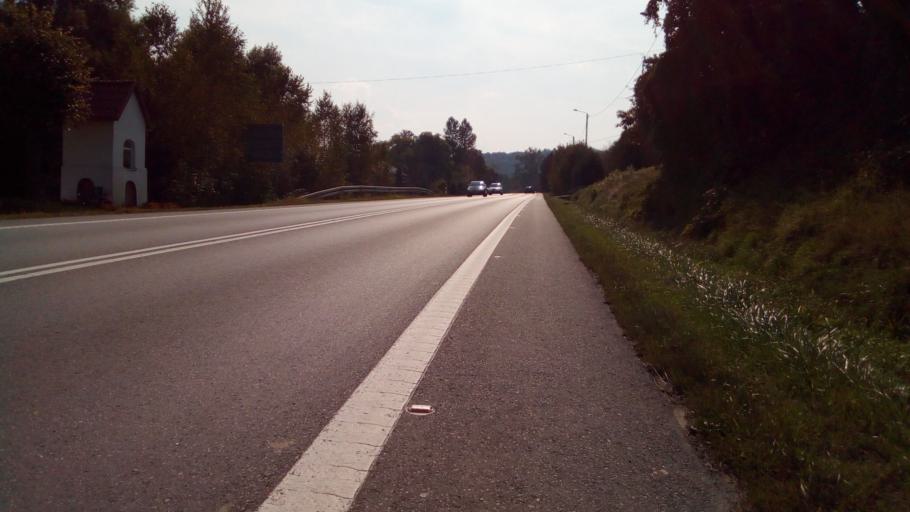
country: PL
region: Subcarpathian Voivodeship
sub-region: Powiat strzyzowski
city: Jawornik
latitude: 49.8479
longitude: 21.8954
